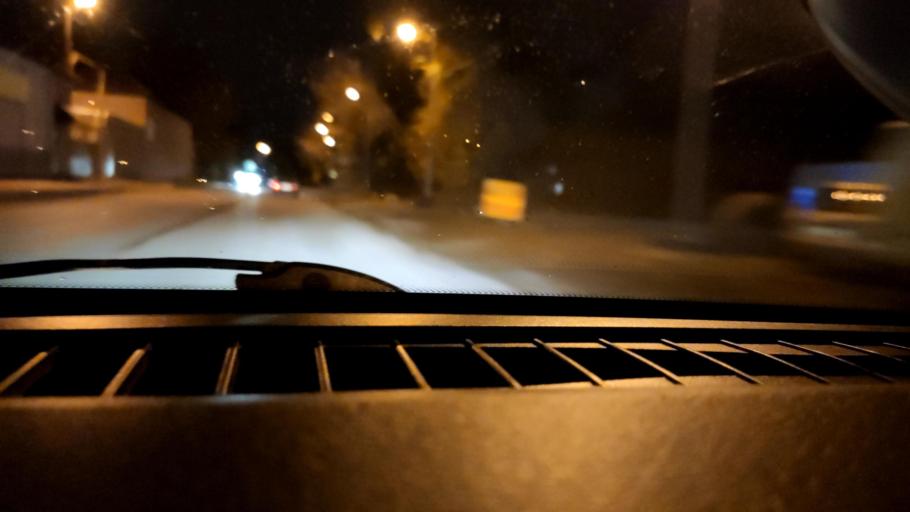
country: RU
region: Samara
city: Petra-Dubrava
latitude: 53.2352
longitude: 50.2941
